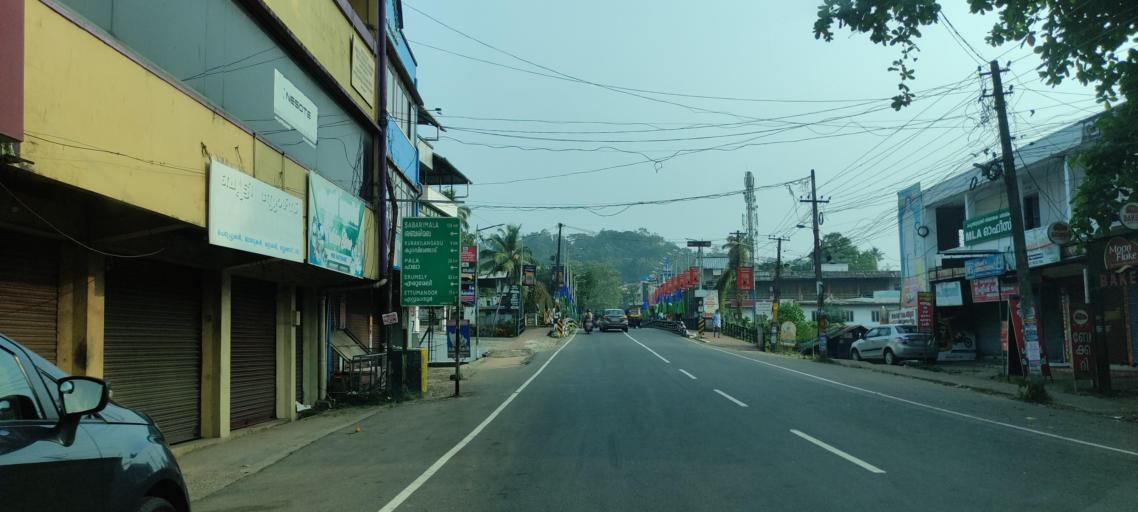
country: IN
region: Kerala
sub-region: Kottayam
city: Vaikam
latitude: 9.7667
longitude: 76.4916
